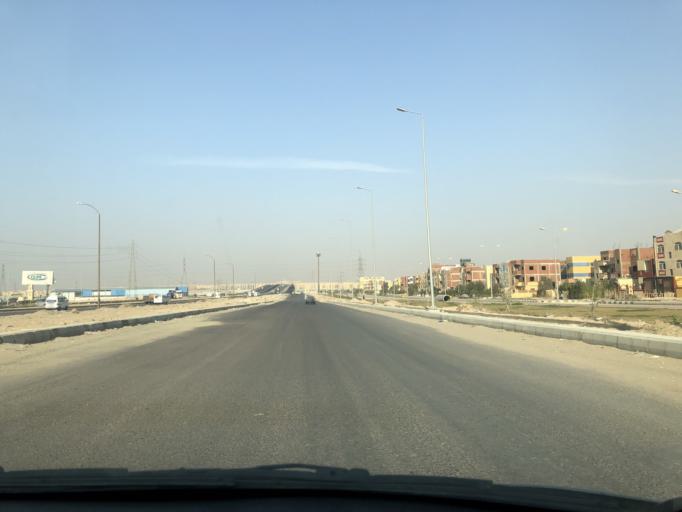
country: EG
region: Al Jizah
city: Madinat Sittah Uktubar
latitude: 29.9066
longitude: 30.9220
